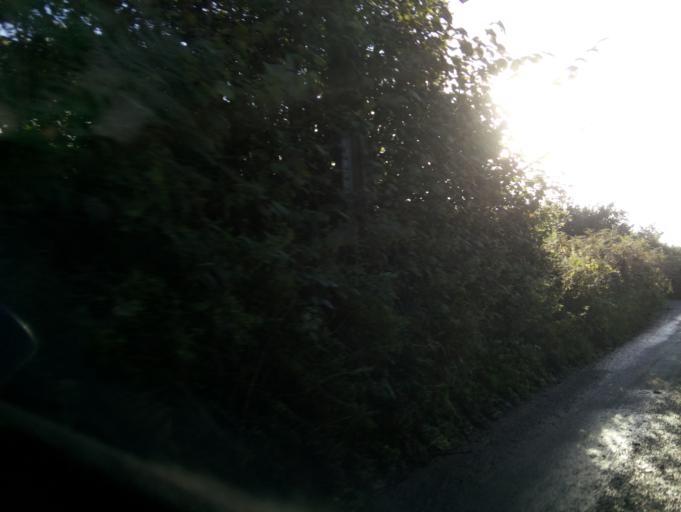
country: GB
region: England
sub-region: Devon
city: Totnes
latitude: 50.3464
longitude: -3.7005
